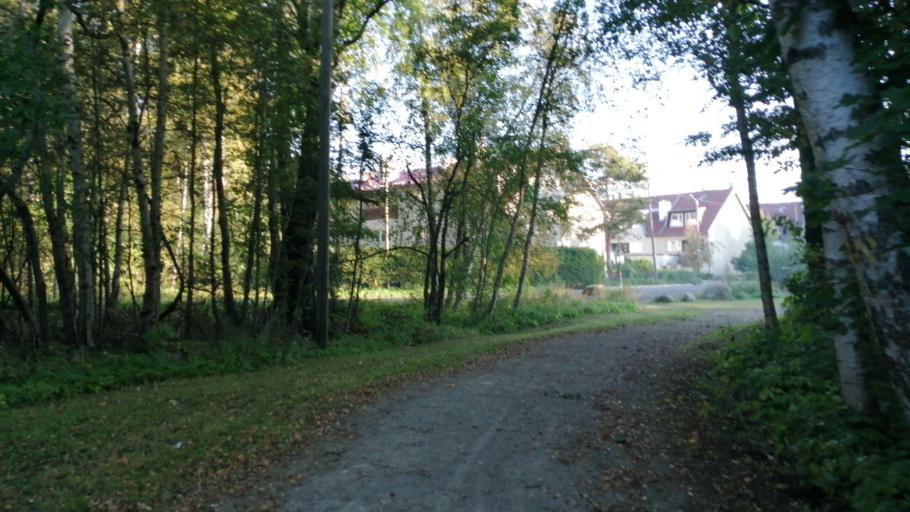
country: EE
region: Harju
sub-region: Saue vald
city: Laagri
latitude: 59.3888
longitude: 24.6460
